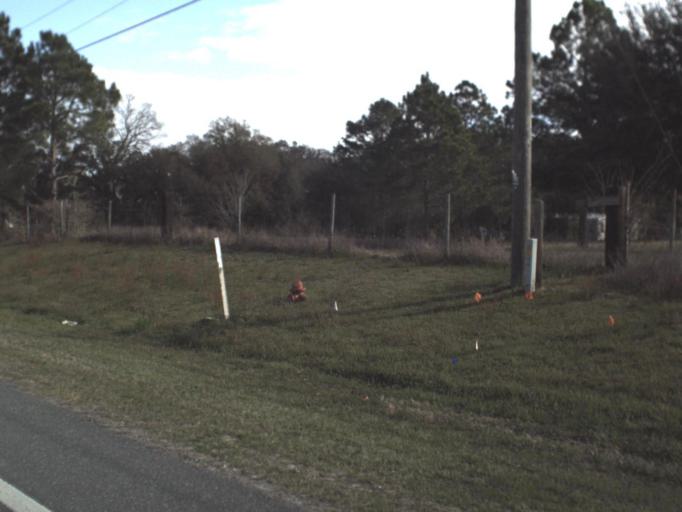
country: US
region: Florida
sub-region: Jackson County
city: Malone
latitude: 30.8885
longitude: -85.1612
